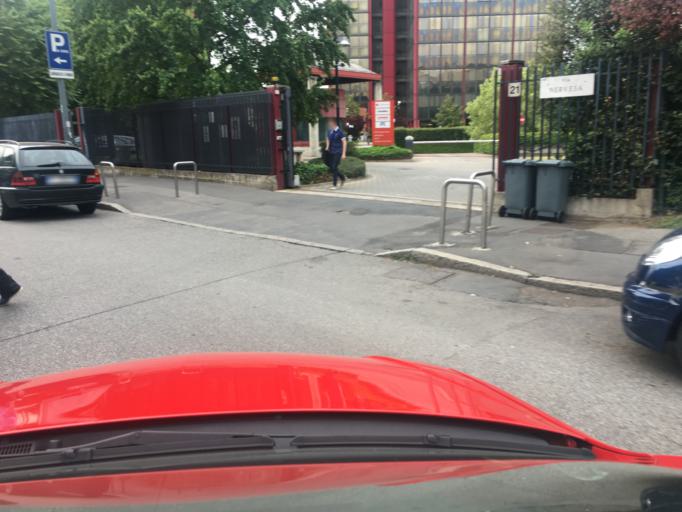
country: IT
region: Lombardy
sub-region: Citta metropolitana di Milano
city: Chiaravalle
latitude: 45.4439
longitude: 9.2184
